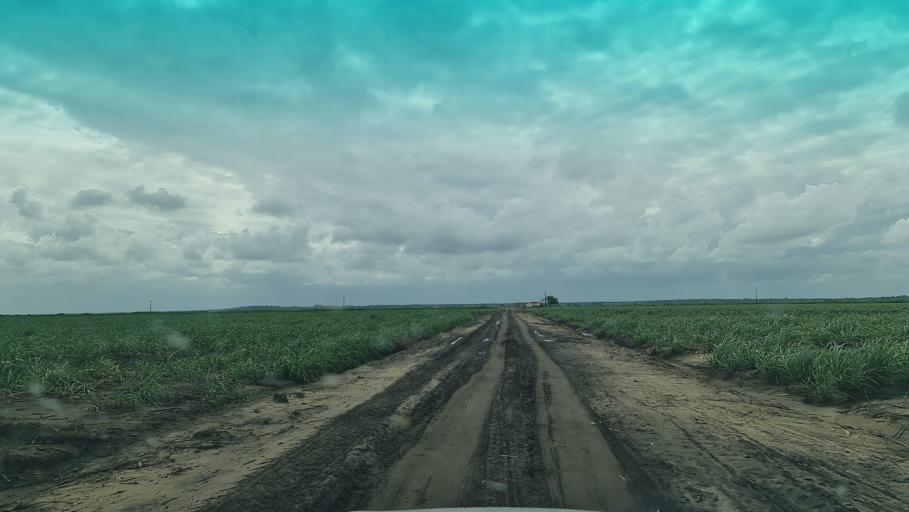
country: MZ
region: Maputo
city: Manhica
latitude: -25.4379
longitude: 32.8451
